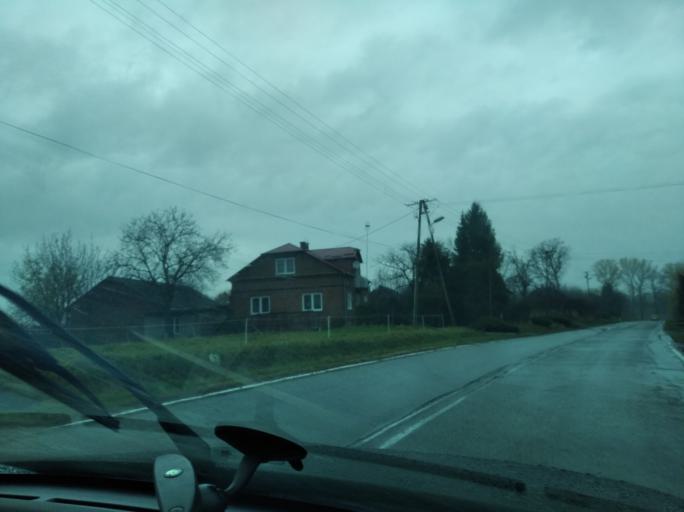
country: PL
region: Subcarpathian Voivodeship
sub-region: Powiat lancucki
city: Albigowa
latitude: 50.0067
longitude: 22.2140
